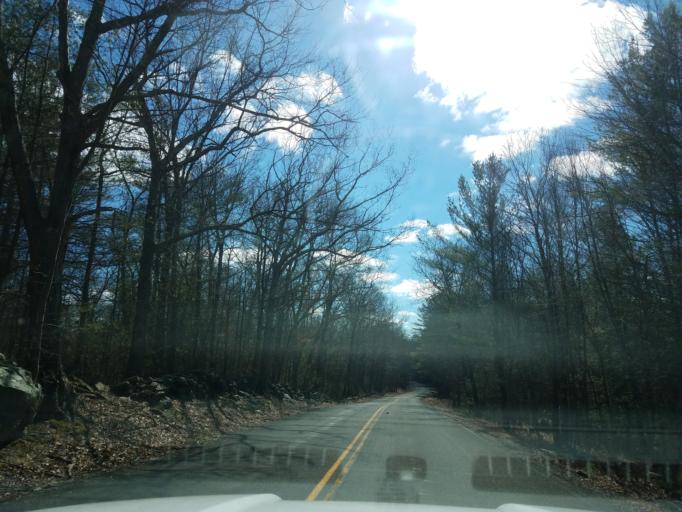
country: US
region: Connecticut
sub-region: Windham County
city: North Grosvenor Dale
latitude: 41.9888
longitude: -71.8737
